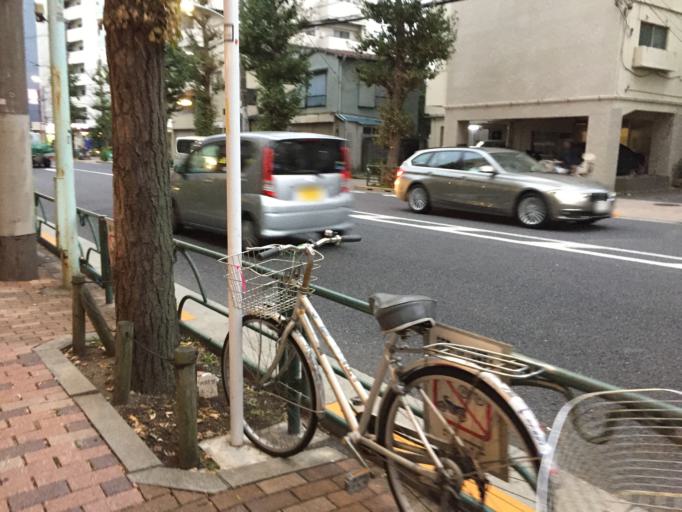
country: JP
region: Tokyo
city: Tokyo
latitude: 35.6422
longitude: 139.6564
